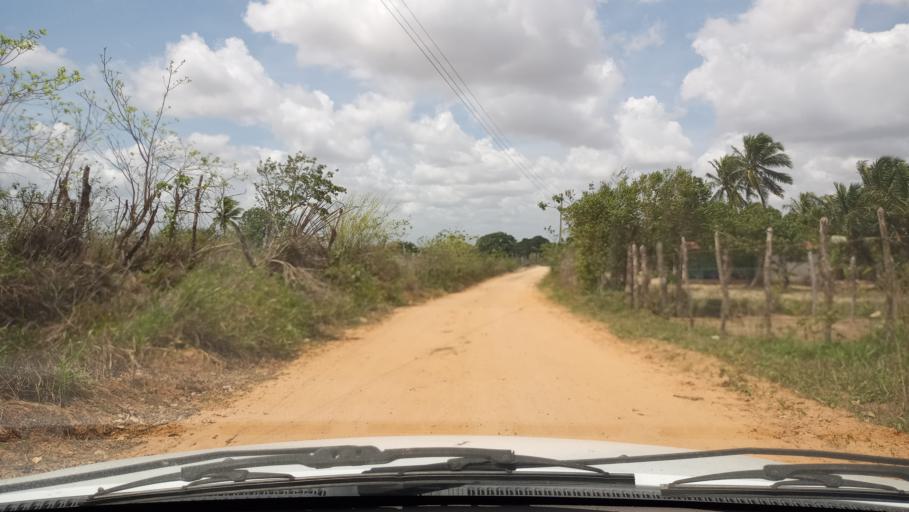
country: BR
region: Rio Grande do Norte
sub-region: Brejinho
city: Brejinho
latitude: -6.2689
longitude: -35.3438
